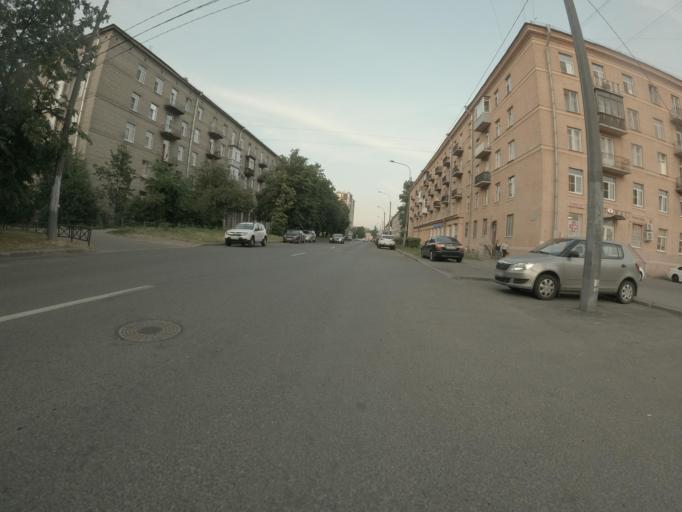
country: RU
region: Leningrad
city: Finlyandskiy
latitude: 59.9709
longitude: 30.3895
